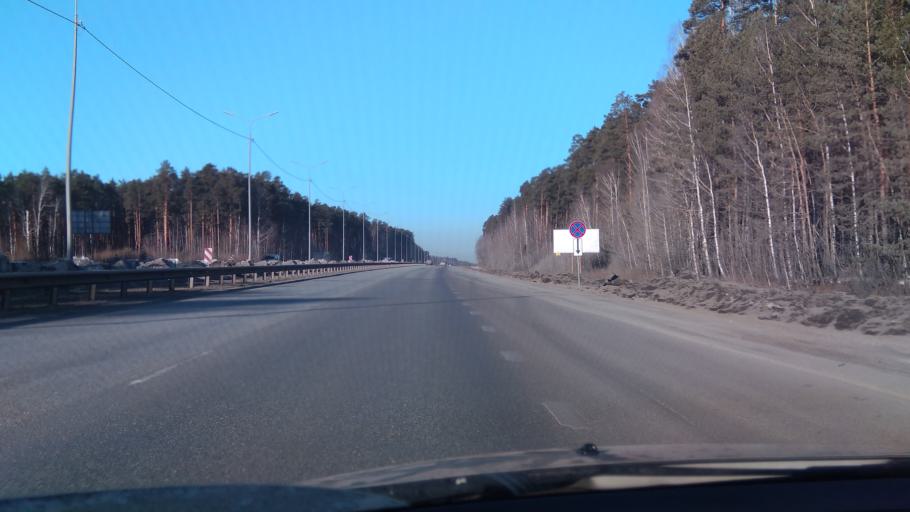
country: RU
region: Sverdlovsk
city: Shirokaya Rechka
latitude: 56.8255
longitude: 60.4625
